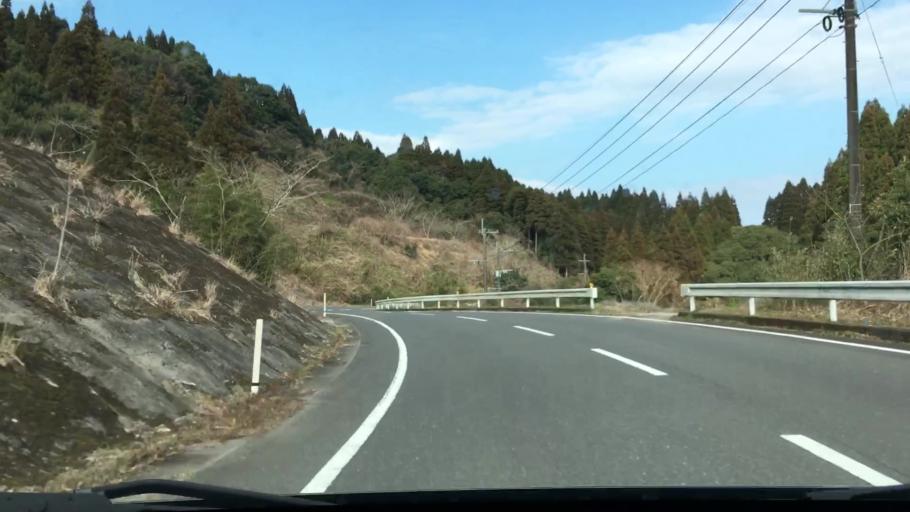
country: JP
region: Miyazaki
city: Kushima
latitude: 31.5696
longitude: 131.2615
